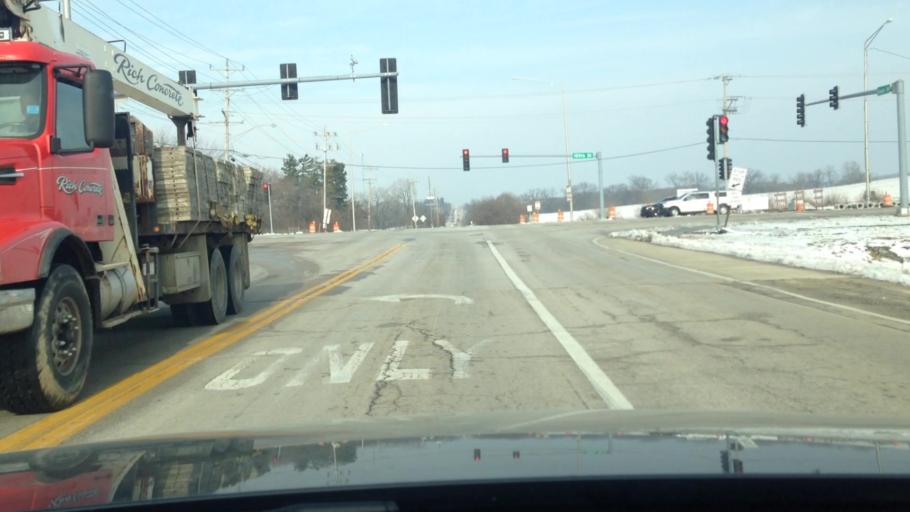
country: US
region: Illinois
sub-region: Will County
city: Lockport
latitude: 41.5977
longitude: -88.0072
